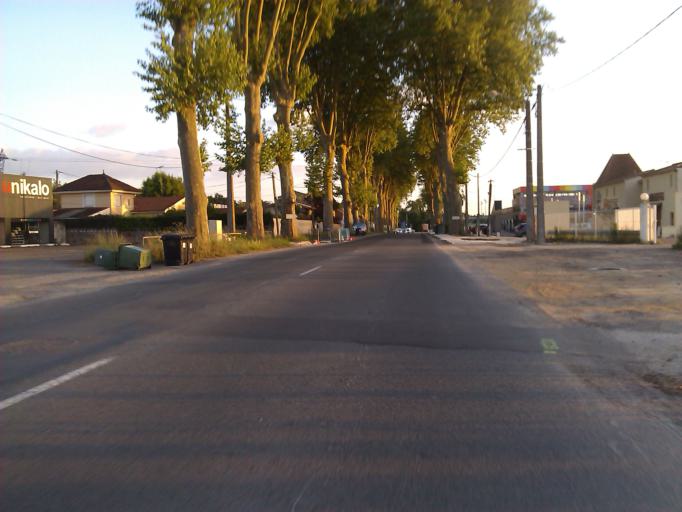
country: FR
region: Aquitaine
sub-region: Departement de la Gironde
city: Carbon-Blanc
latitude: 44.9012
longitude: -0.4921
